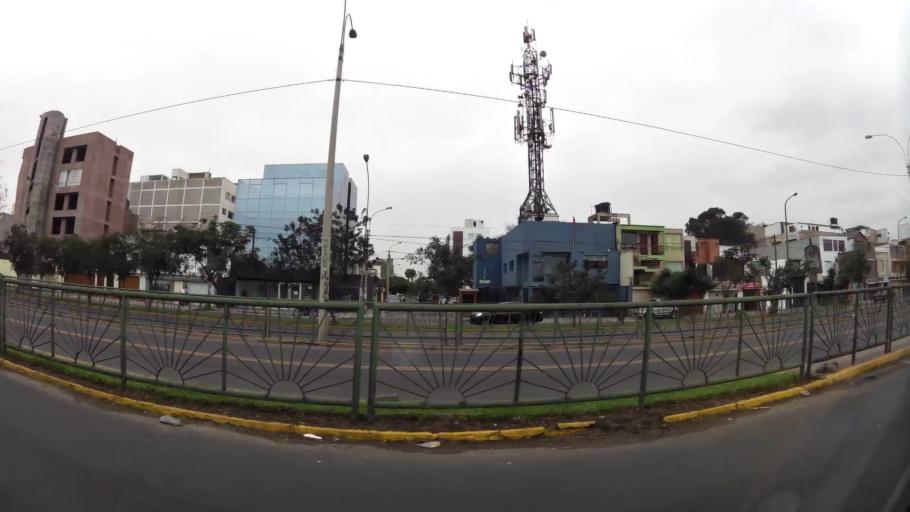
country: PE
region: Lima
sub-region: Lima
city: Surco
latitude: -12.1255
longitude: -77.0036
